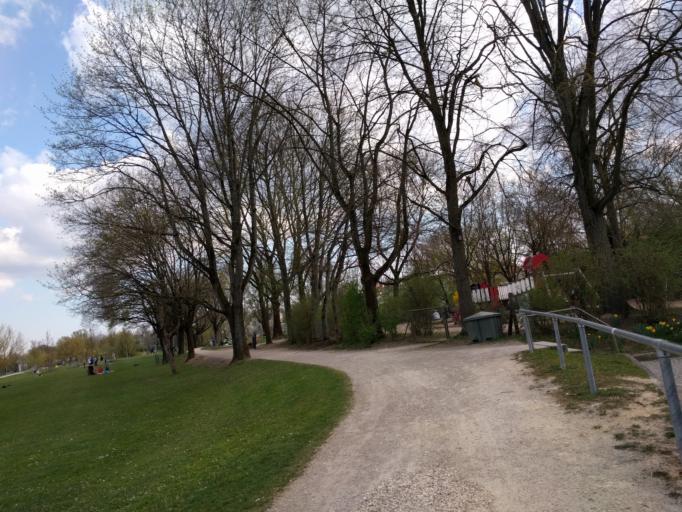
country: DE
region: Bavaria
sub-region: Upper Palatinate
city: Regensburg
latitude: 49.0248
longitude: 12.1039
